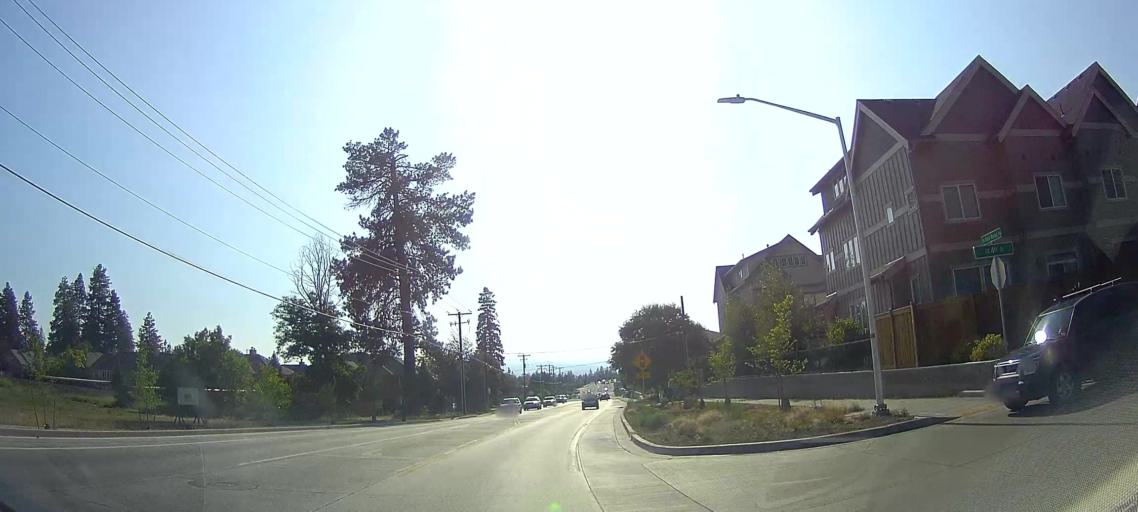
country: US
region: Oregon
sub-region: Deschutes County
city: Bend
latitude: 44.0385
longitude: -121.3010
